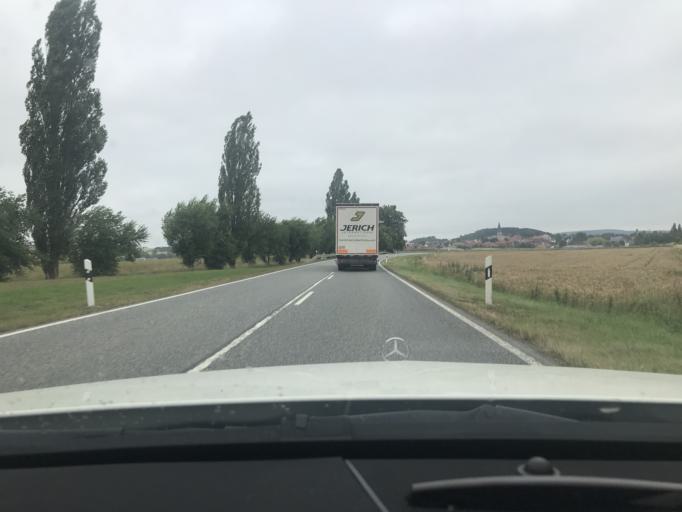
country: DE
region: Thuringia
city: Leinefelde
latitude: 51.3975
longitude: 10.3295
